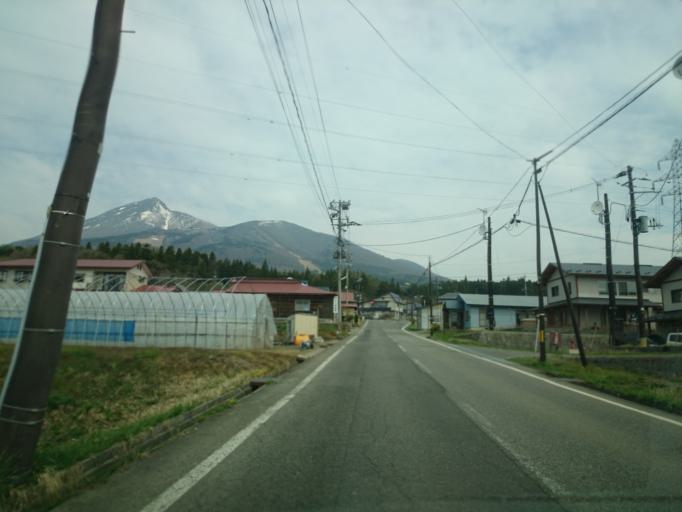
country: JP
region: Fukushima
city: Inawashiro
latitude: 37.5635
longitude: 140.0995
